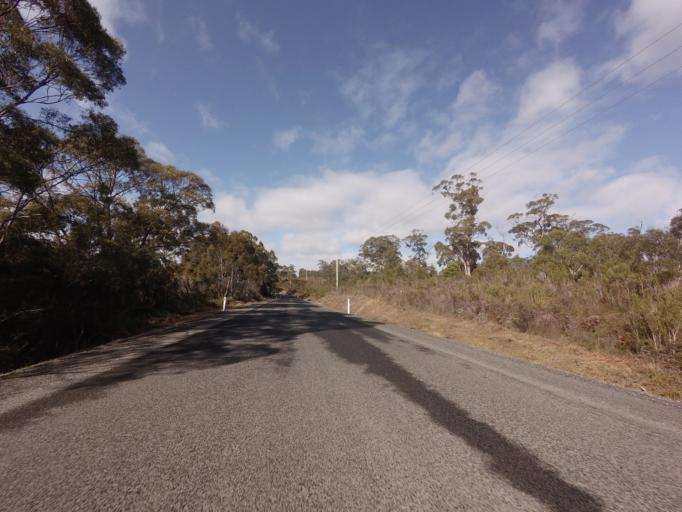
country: AU
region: Tasmania
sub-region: Huon Valley
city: Geeveston
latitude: -43.4225
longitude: 146.9048
